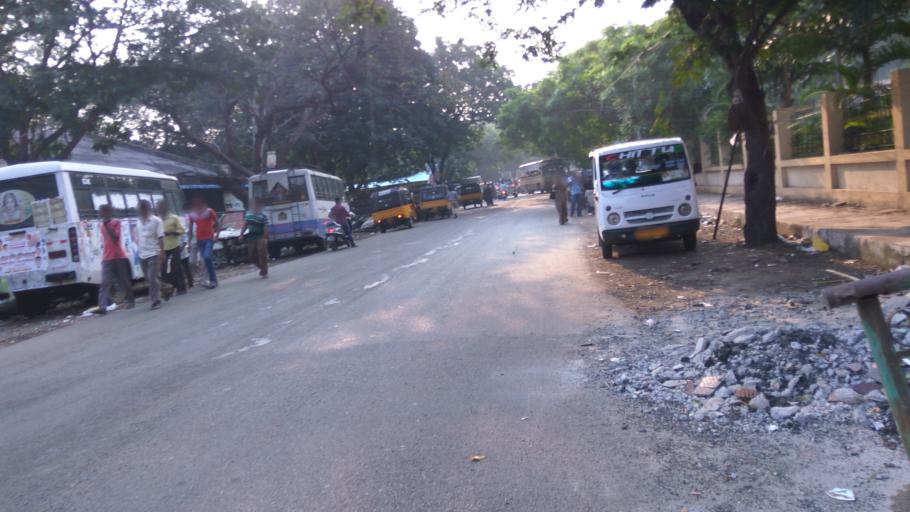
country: IN
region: Tamil Nadu
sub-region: Kancheepuram
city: Alandur
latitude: 13.0098
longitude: 80.2103
